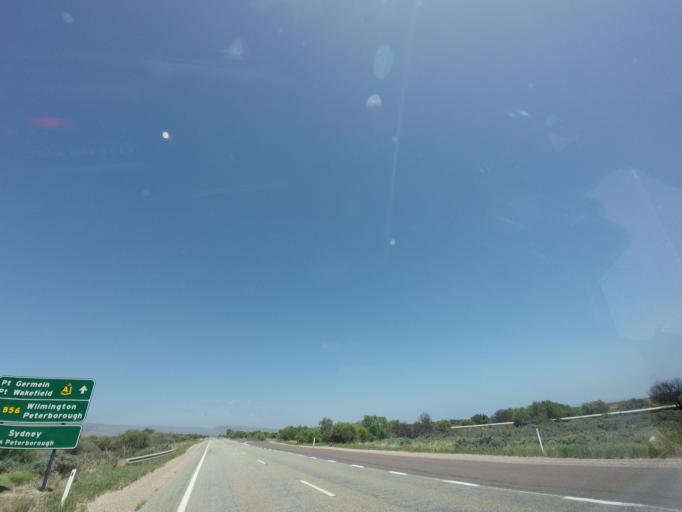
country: AU
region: South Australia
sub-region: Port Augusta
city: Port Augusta
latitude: -32.6246
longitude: 137.9140
